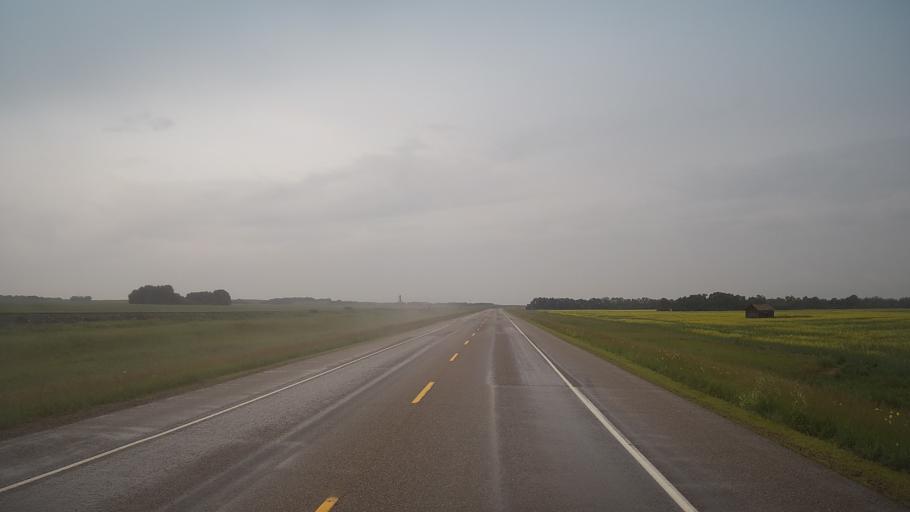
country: CA
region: Saskatchewan
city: Wilkie
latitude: 52.2349
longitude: -108.5512
